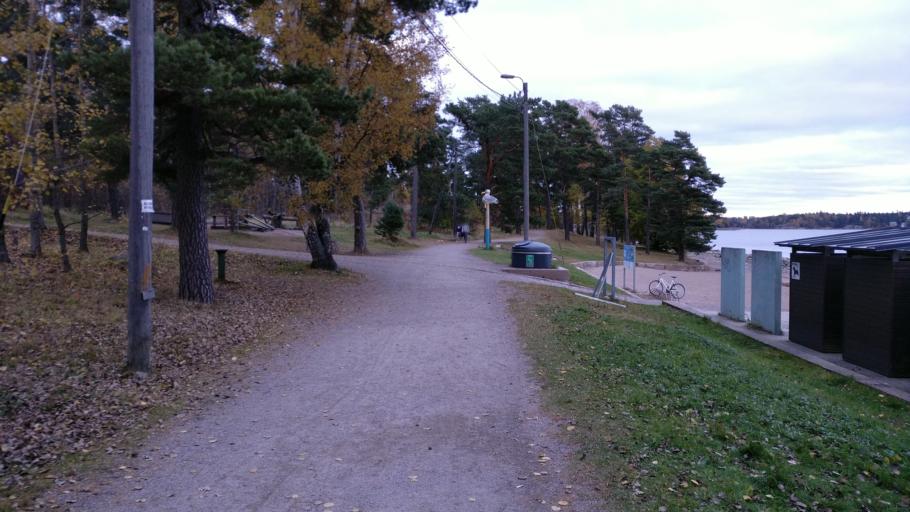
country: FI
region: Uusimaa
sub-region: Helsinki
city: Helsinki
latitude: 60.1790
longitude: 24.9926
